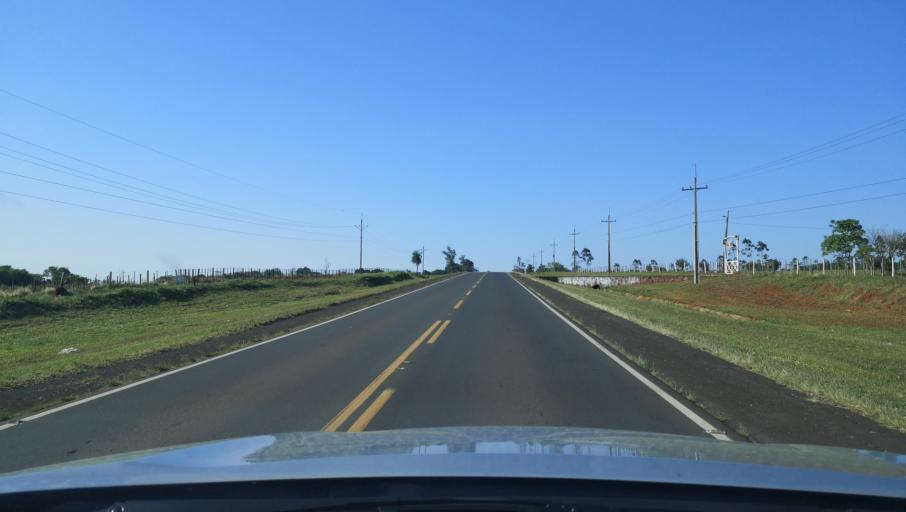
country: PY
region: Misiones
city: Santa Maria
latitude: -26.8291
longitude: -57.0305
